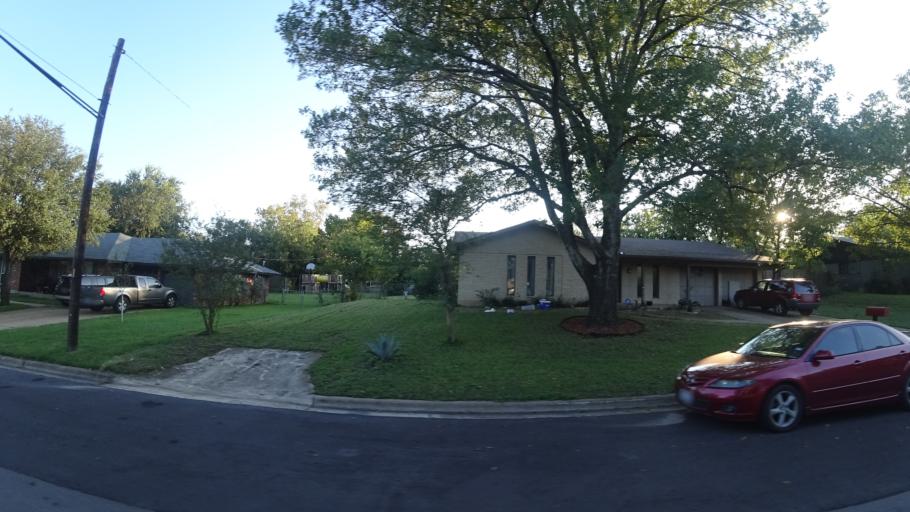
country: US
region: Texas
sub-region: Travis County
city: Wells Branch
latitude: 30.3674
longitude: -97.6762
